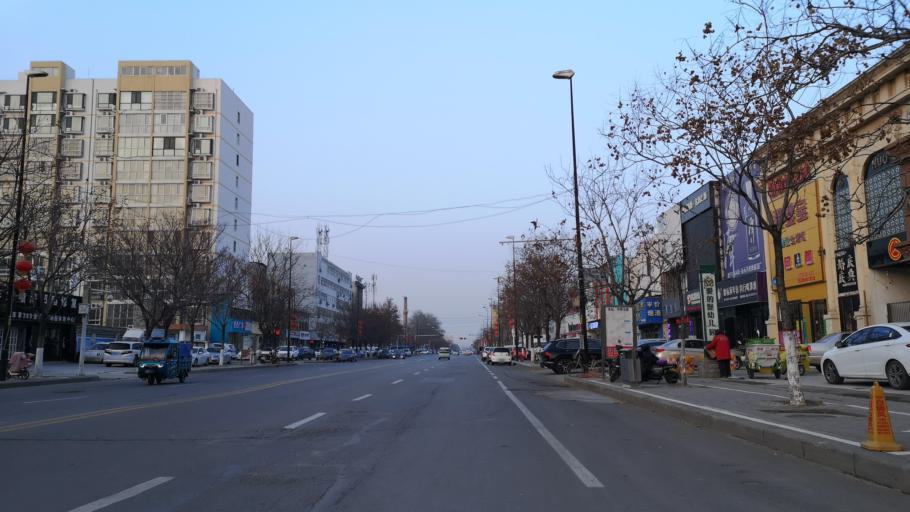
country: CN
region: Henan Sheng
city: Zhongyuanlu
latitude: 35.7759
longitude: 115.0600
